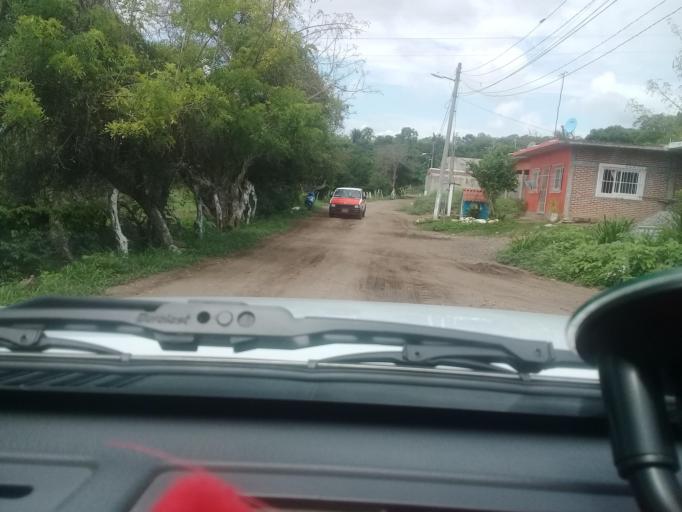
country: MX
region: Veracruz
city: Paso de Ovejas
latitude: 19.2927
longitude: -96.4348
